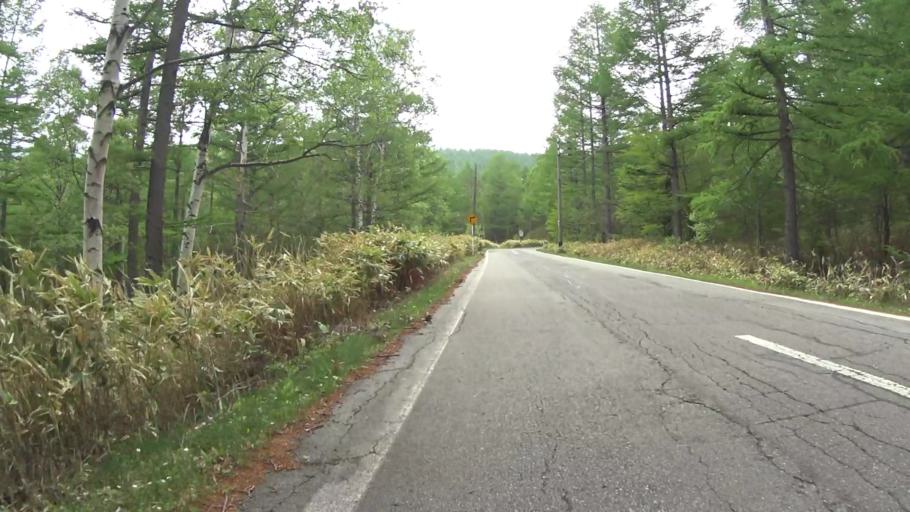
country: JP
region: Nagano
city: Saku
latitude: 36.0639
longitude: 138.3890
